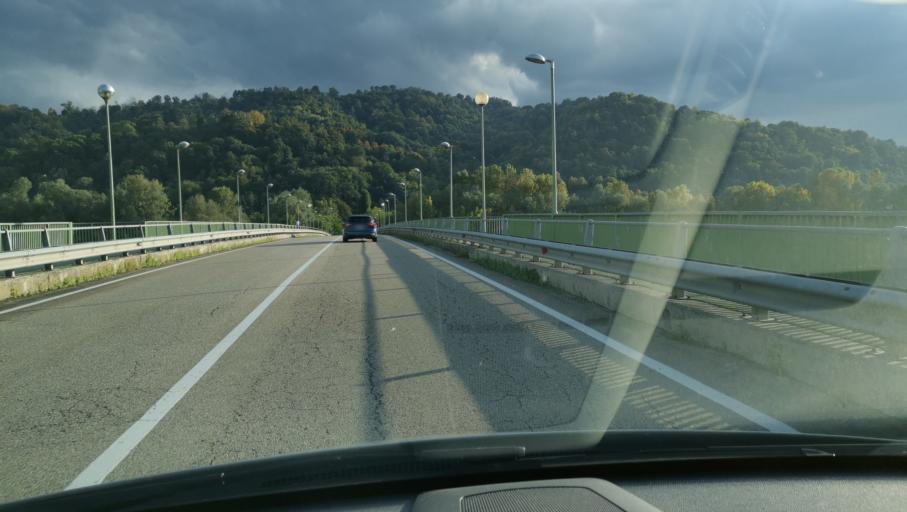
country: IT
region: Piedmont
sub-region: Provincia di Torino
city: Chivasso
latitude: 45.1817
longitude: 7.8902
